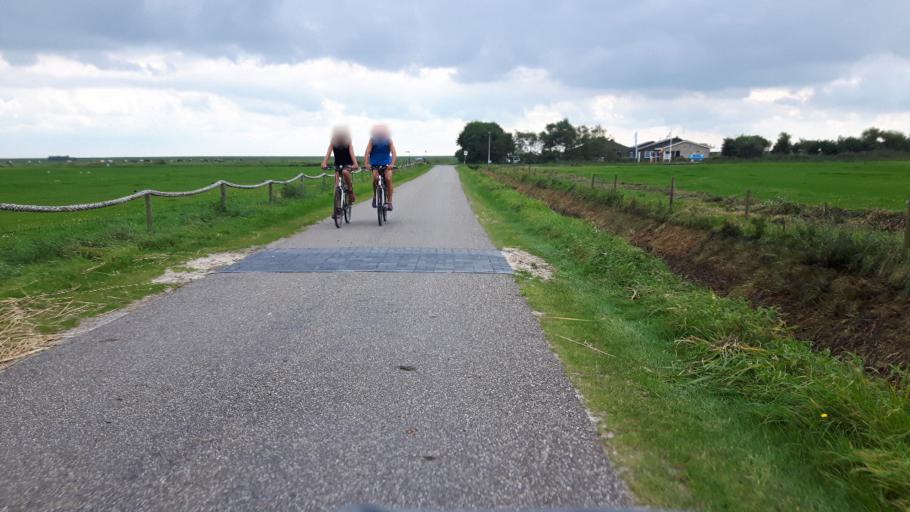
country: NL
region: Friesland
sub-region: Gemeente Ameland
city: Nes
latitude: 53.4509
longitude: 5.8180
